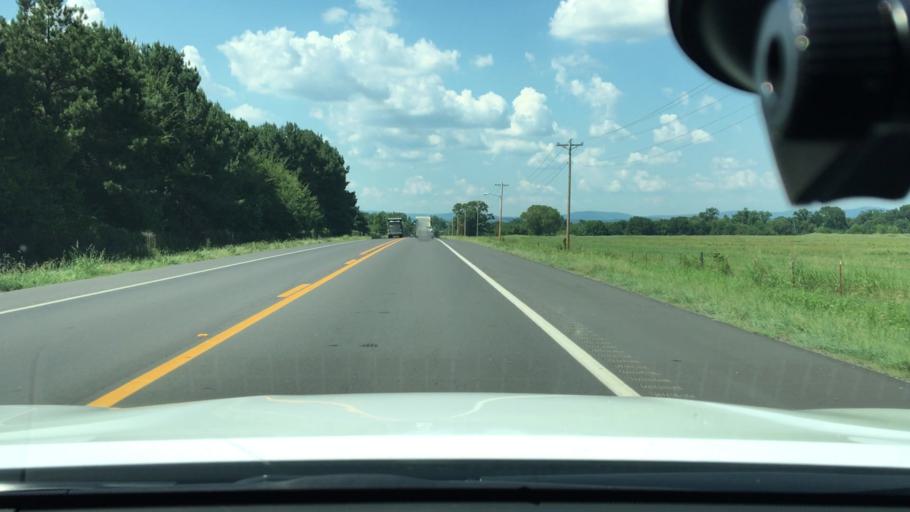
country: US
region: Arkansas
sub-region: Johnson County
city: Clarksville
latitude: 35.4385
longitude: -93.5293
